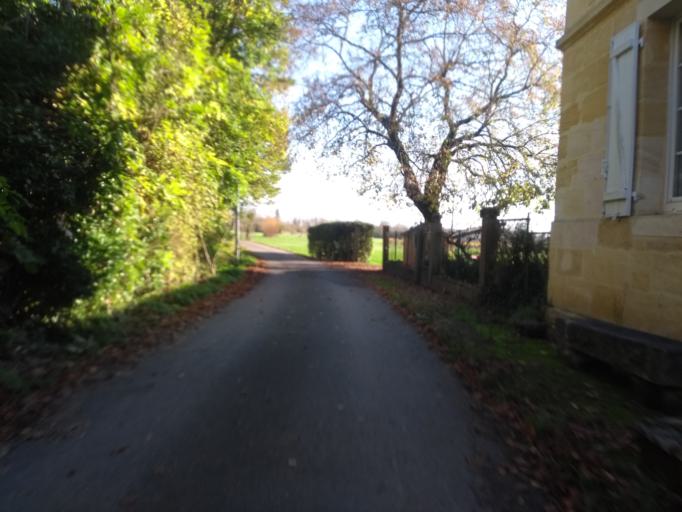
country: FR
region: Aquitaine
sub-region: Departement de la Gironde
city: Cambes
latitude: 44.7316
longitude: -0.4846
